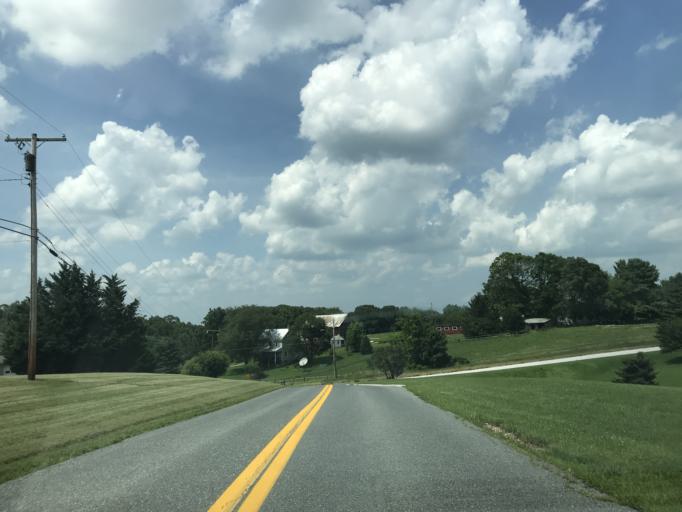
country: US
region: Maryland
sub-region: Carroll County
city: Hampstead
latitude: 39.6158
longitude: -76.7638
